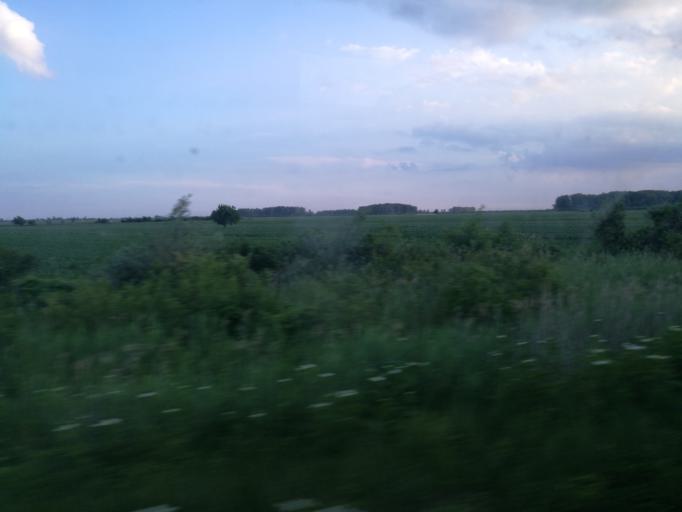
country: RO
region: Dambovita
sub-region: Comuna Contesti
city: Contesti
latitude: 44.6560
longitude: 25.6578
